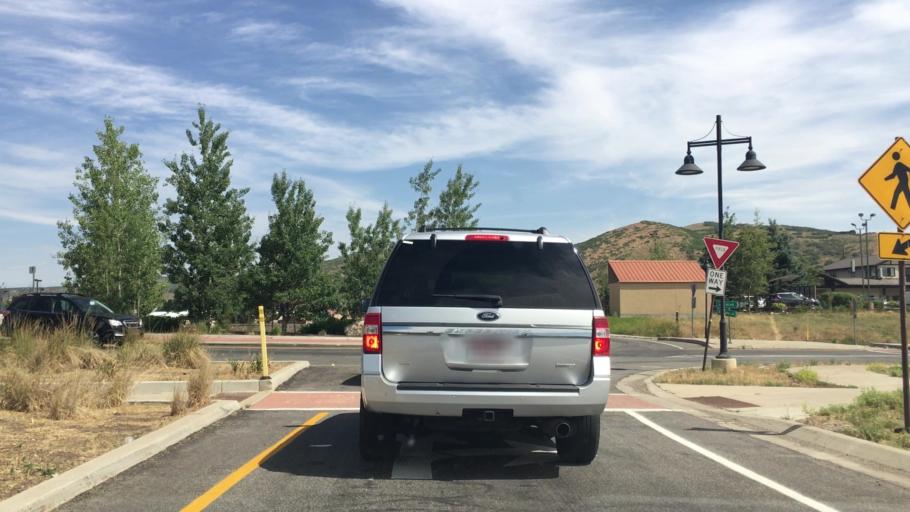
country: US
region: Utah
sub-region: Summit County
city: Snyderville
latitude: 40.7241
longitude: -111.5474
